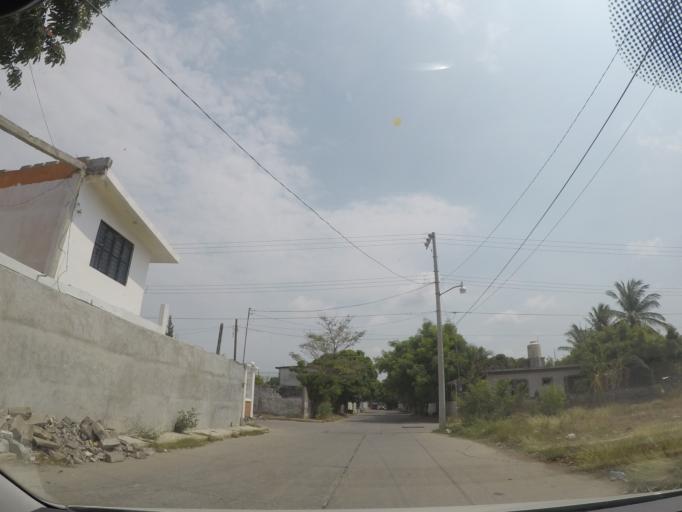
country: MX
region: Oaxaca
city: El Espinal
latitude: 16.4807
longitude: -95.0388
